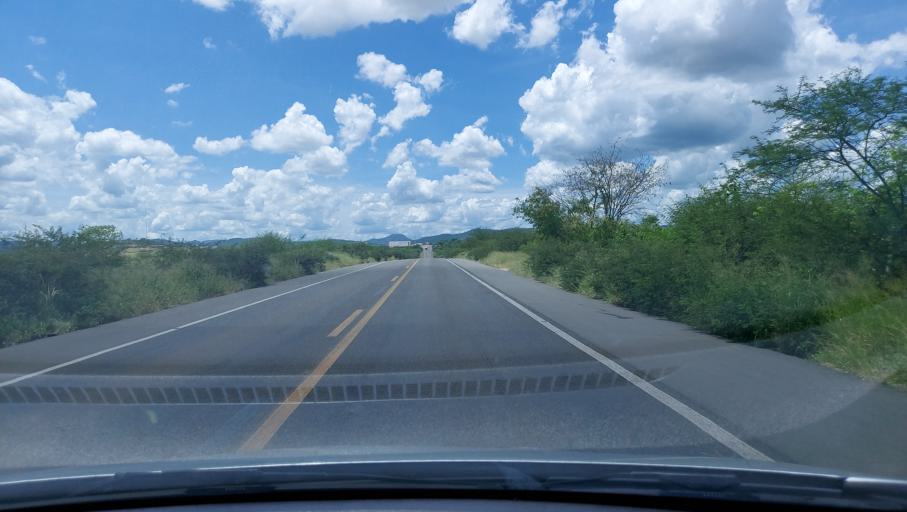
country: BR
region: Bahia
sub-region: Itaberaba
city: Itaberaba
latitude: -12.5210
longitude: -40.2667
